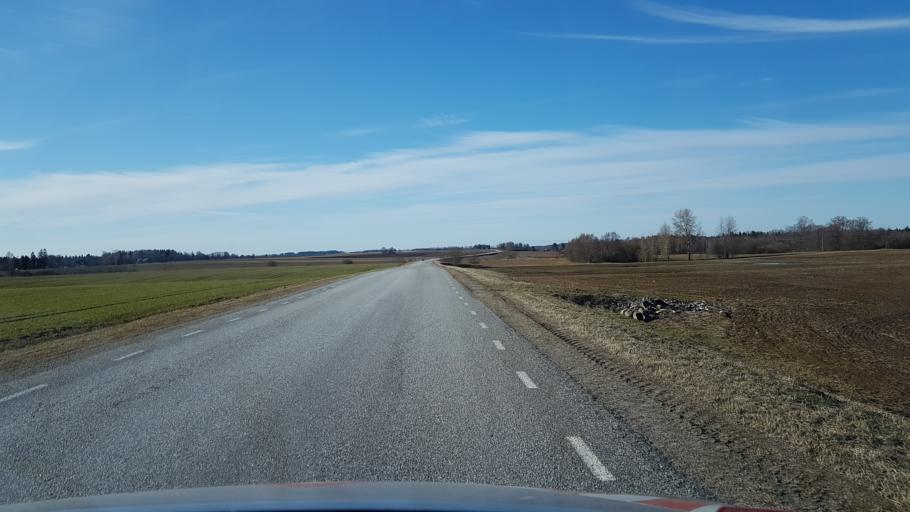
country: EE
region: Laeaene-Virumaa
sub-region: Kadrina vald
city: Kadrina
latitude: 59.3130
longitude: 26.1539
